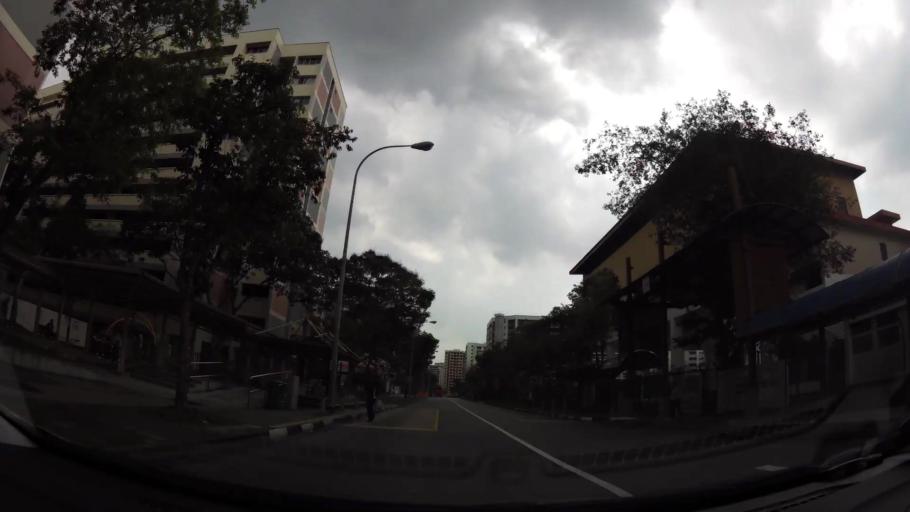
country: SG
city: Singapore
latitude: 1.3535
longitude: 103.9345
